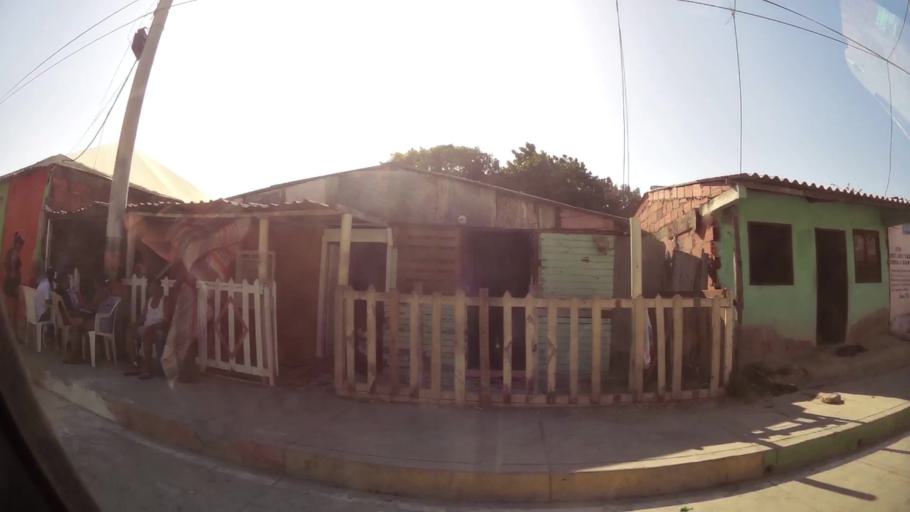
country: CO
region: Bolivar
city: Cartagena
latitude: 10.4157
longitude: -75.5182
